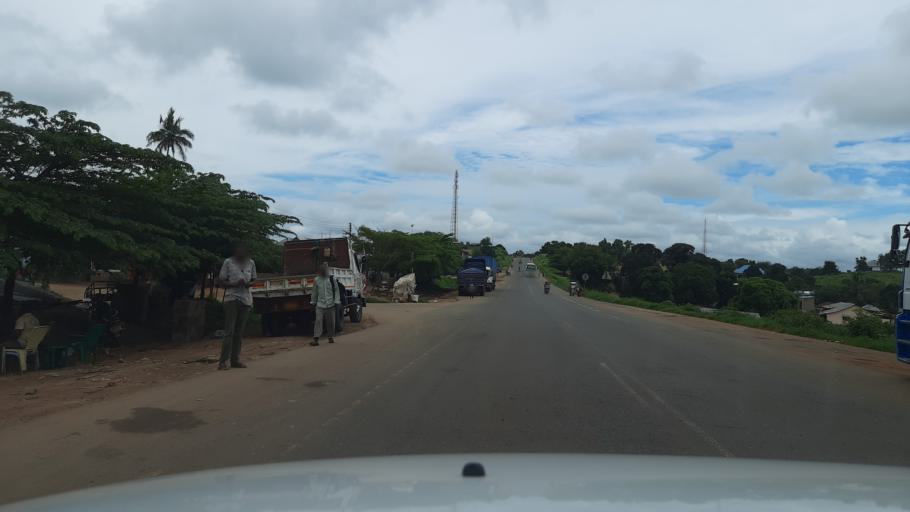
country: TZ
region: Pwani
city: Lugoba
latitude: -6.0797
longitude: 38.2434
